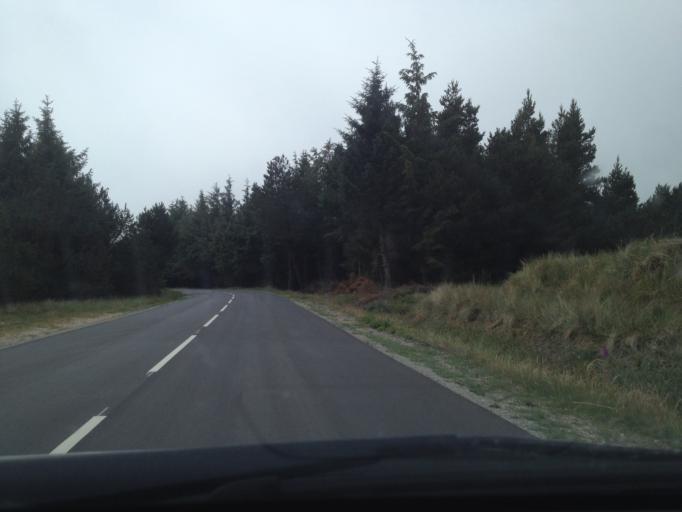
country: DK
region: South Denmark
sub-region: Varde Kommune
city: Oksbol
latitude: 55.5591
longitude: 8.1664
